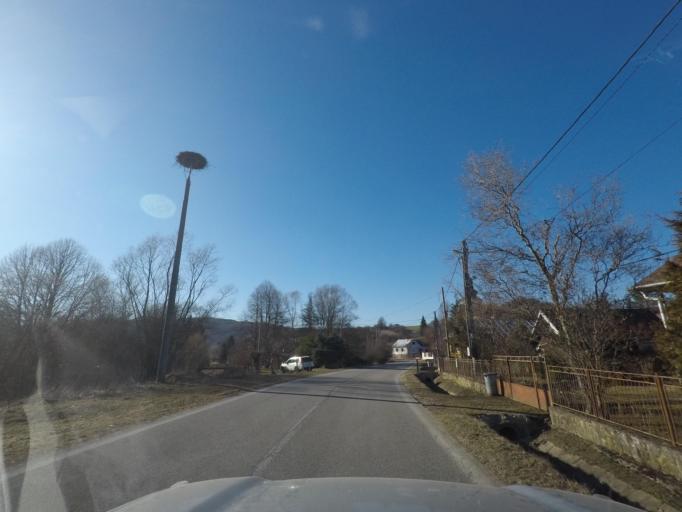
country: PL
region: Subcarpathian Voivodeship
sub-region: Powiat sanocki
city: Komancza
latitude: 49.1637
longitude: 22.0405
